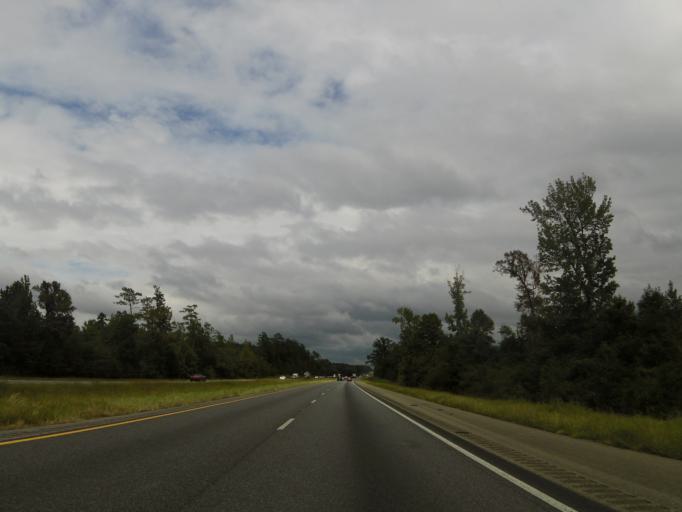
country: US
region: Alabama
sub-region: Escambia County
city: Brewton
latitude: 31.3014
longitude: -87.1720
